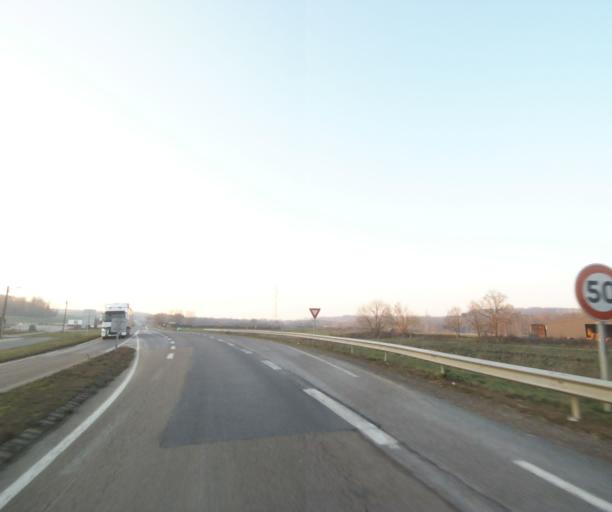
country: FR
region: Lorraine
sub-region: Departement de la Meuse
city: Ancerville
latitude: 48.6049
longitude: 5.0282
